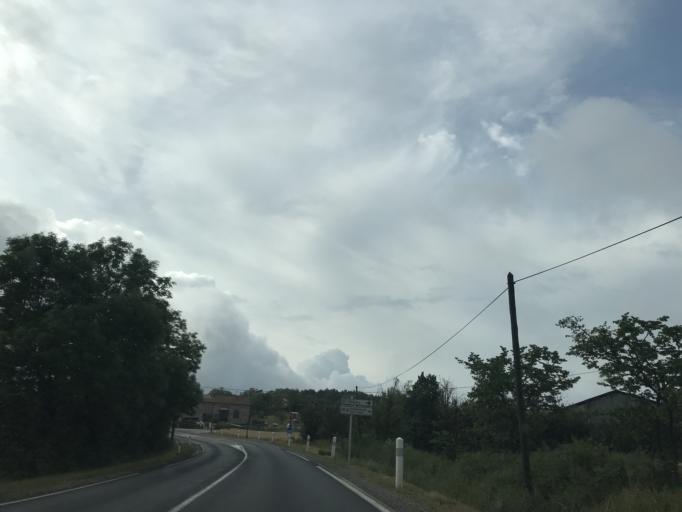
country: FR
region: Auvergne
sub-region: Departement de la Haute-Loire
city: Polignac
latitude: 45.0829
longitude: 3.8202
